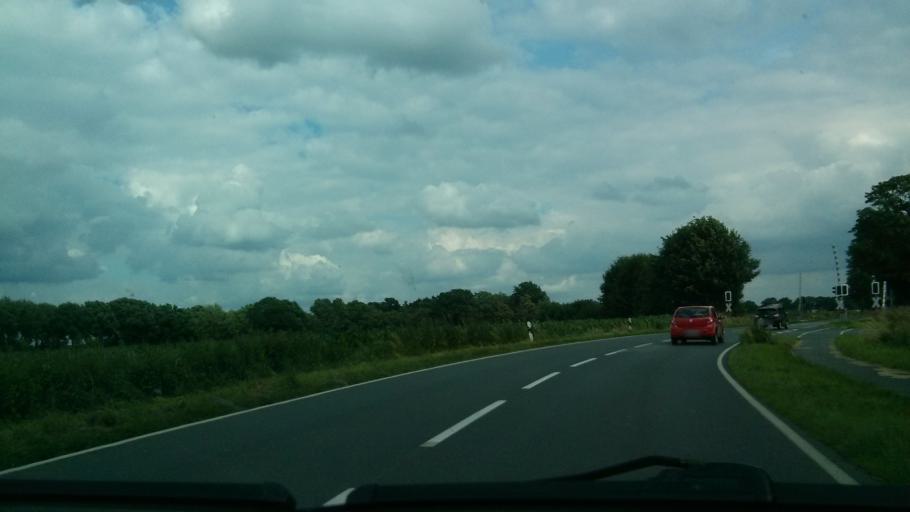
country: DE
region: Lower Saxony
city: Elmlohe
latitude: 53.5175
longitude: 8.7489
